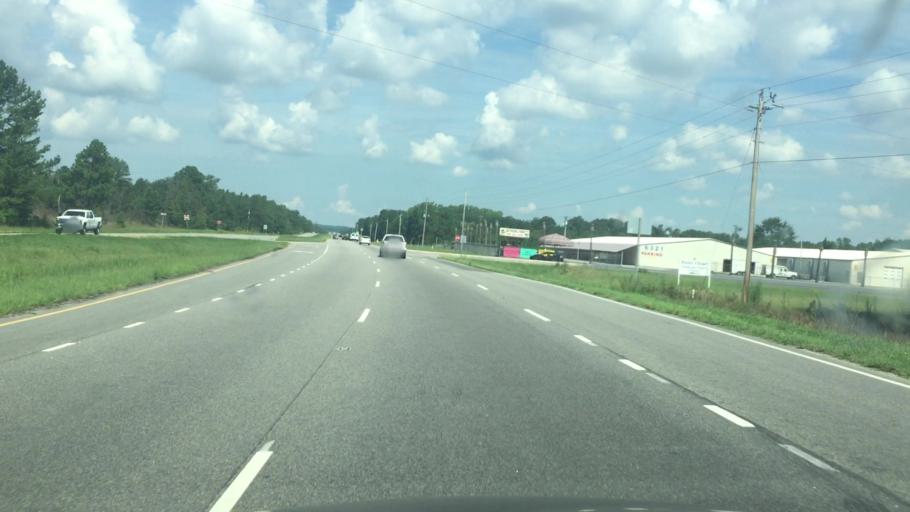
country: US
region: North Carolina
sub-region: Scotland County
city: Laurel Hill
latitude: 34.8364
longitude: -79.5970
